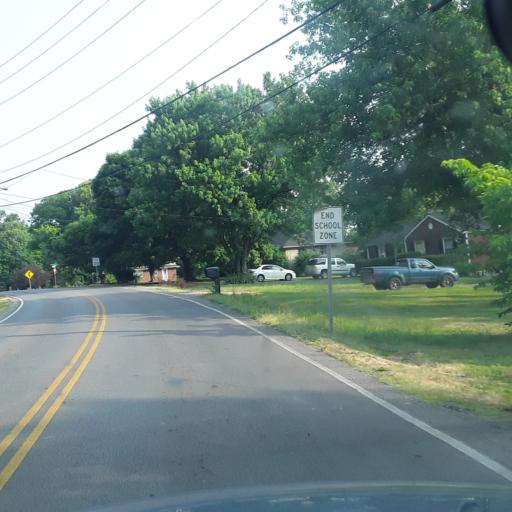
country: US
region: Tennessee
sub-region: Davidson County
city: Oak Hill
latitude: 36.0614
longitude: -86.7215
